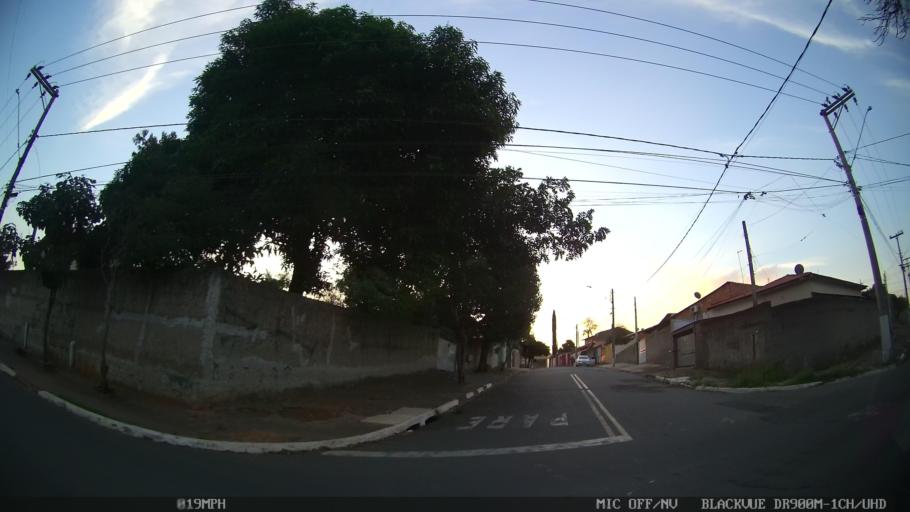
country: BR
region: Sao Paulo
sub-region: Hortolandia
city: Hortolandia
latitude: -22.8602
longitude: -47.2124
